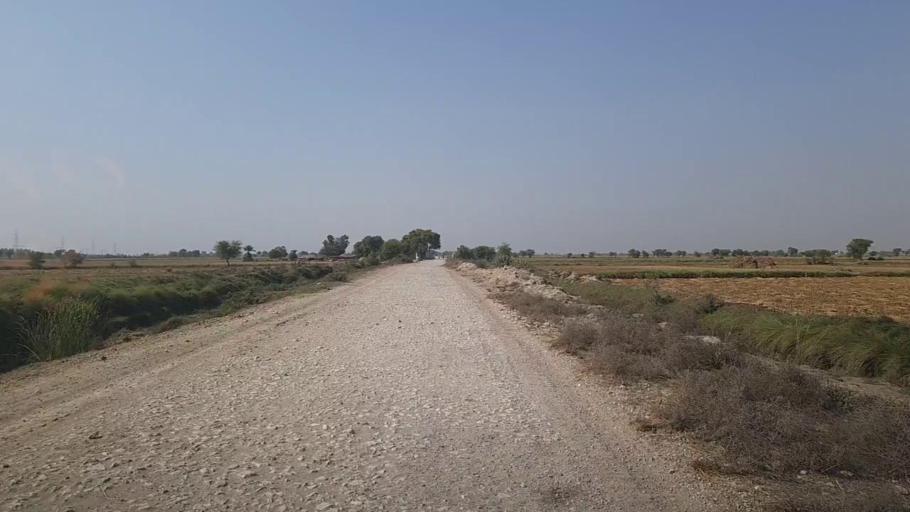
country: PK
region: Sindh
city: Kandhkot
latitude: 28.3902
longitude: 69.2878
